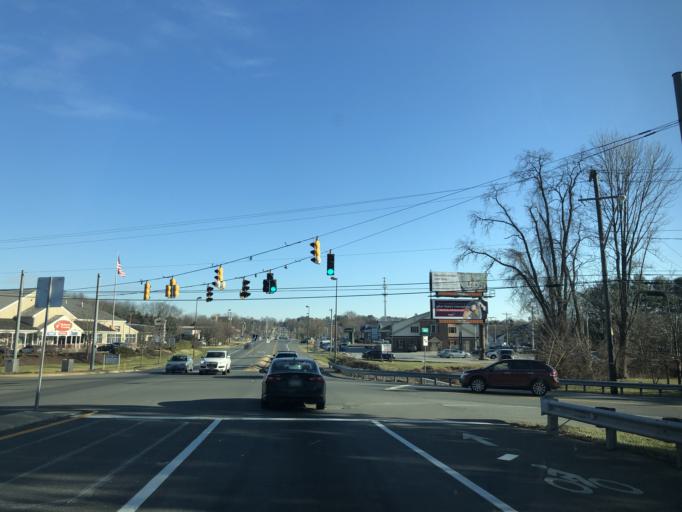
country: US
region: Delaware
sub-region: New Castle County
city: Hockessin
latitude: 39.7900
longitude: -75.7004
